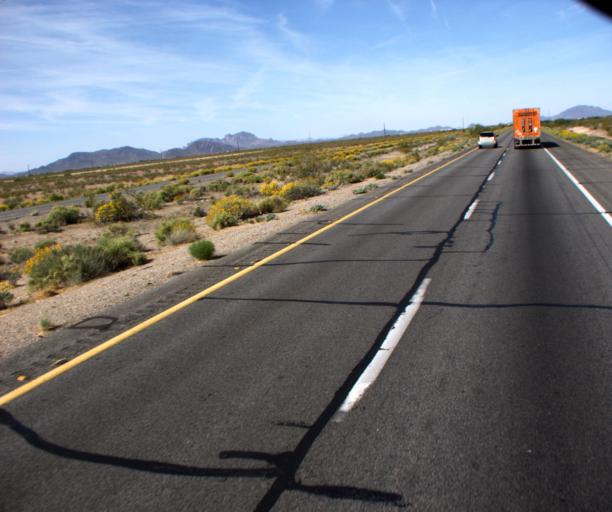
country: US
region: Arizona
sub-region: Maricopa County
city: Buckeye
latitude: 33.4726
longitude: -112.8254
